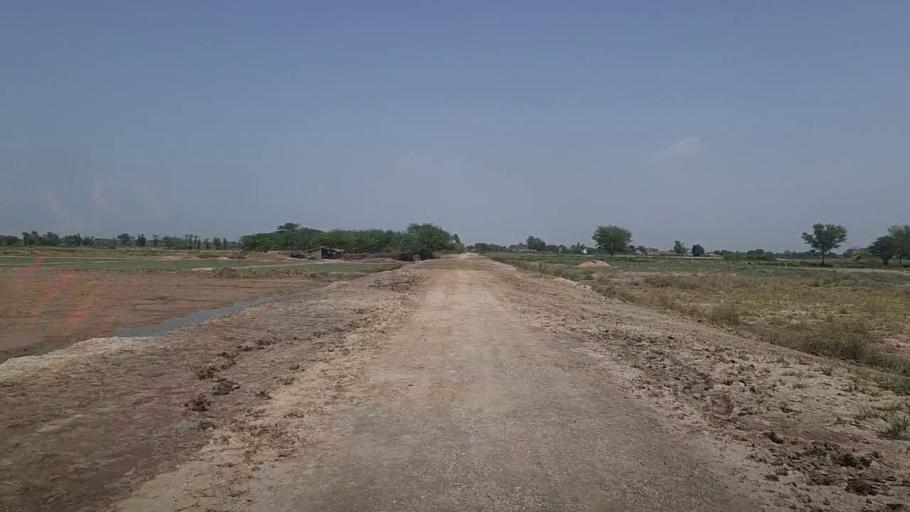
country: PK
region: Sindh
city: Pad Idan
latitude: 26.8444
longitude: 68.3161
